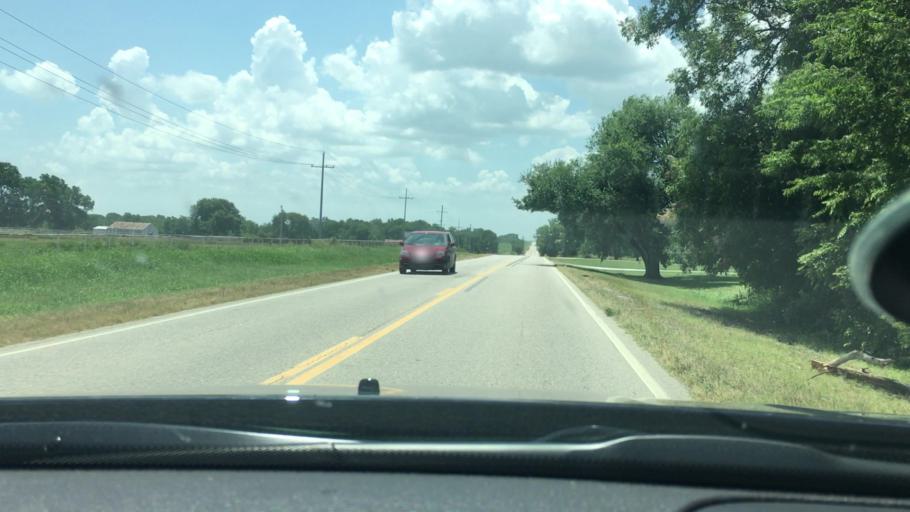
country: US
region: Oklahoma
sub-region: Pontotoc County
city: Ada
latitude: 34.6913
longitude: -96.6349
